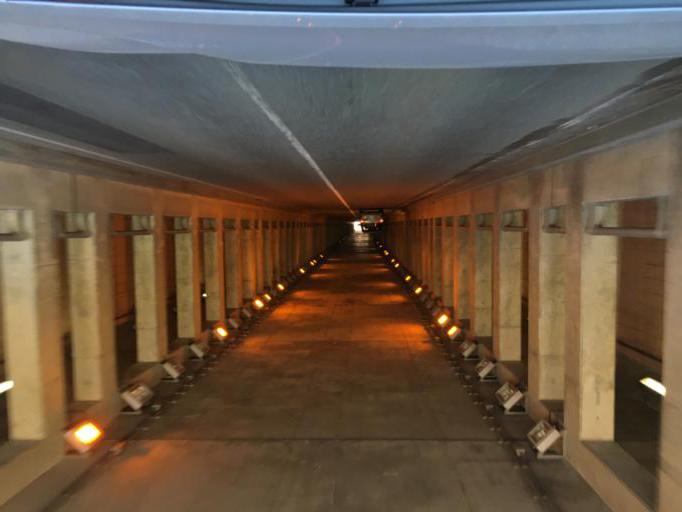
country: JP
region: Yamagata
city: Tsuruoka
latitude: 38.8128
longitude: 139.7790
